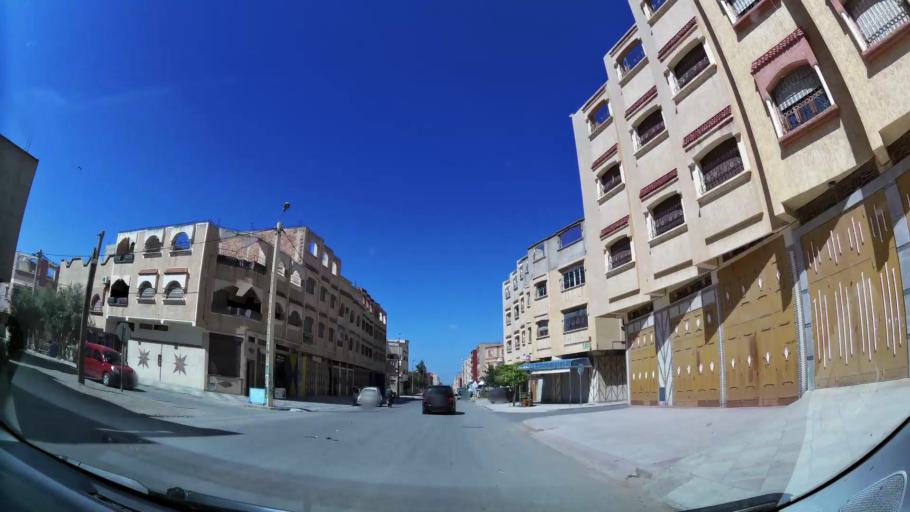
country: MA
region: Oriental
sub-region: Oujda-Angad
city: Oujda
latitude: 34.6854
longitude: -1.9420
